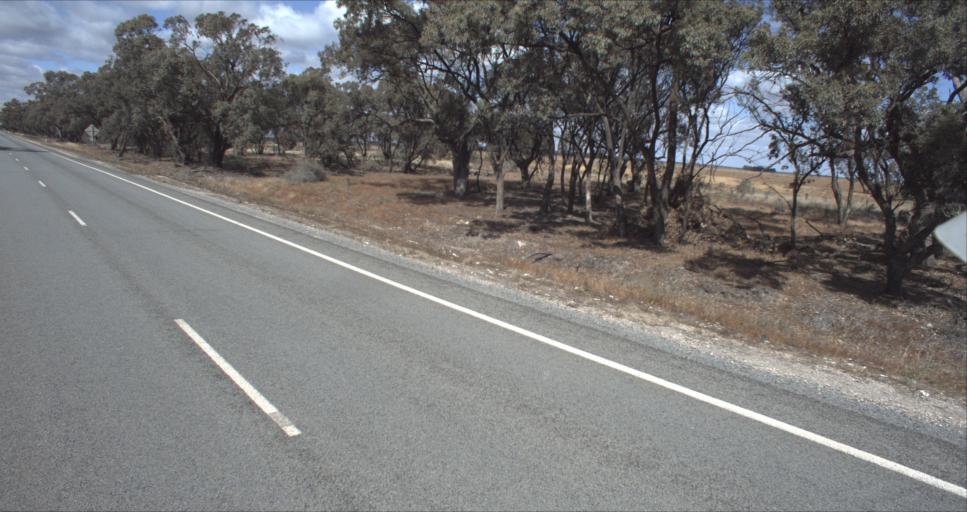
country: AU
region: New South Wales
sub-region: Murrumbidgee Shire
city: Darlington Point
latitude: -34.5626
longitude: 146.1687
